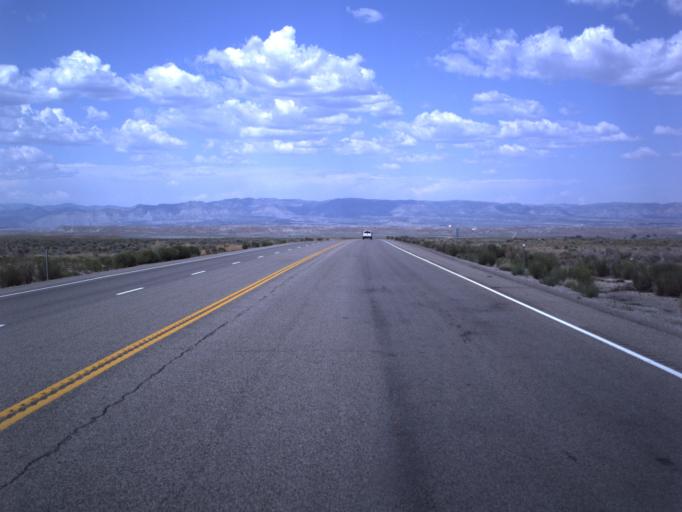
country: US
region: Utah
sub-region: Carbon County
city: Price
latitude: 39.4800
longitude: -110.8527
